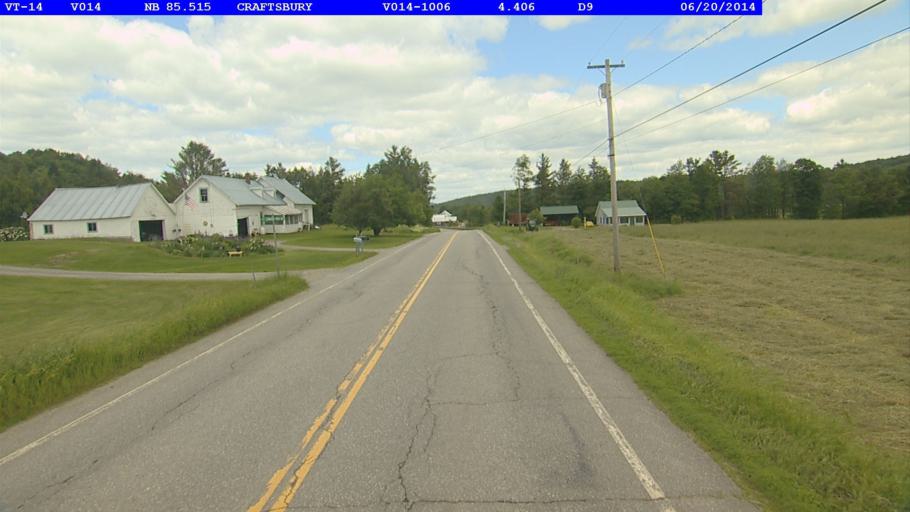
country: US
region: Vermont
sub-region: Caledonia County
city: Hardwick
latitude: 44.6541
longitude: -72.4051
